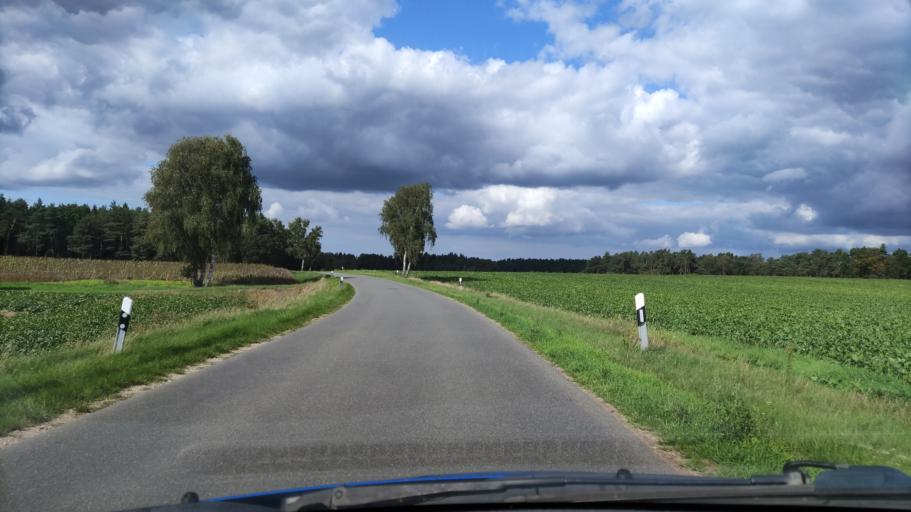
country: DE
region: Lower Saxony
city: Weste
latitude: 53.0335
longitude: 10.7231
